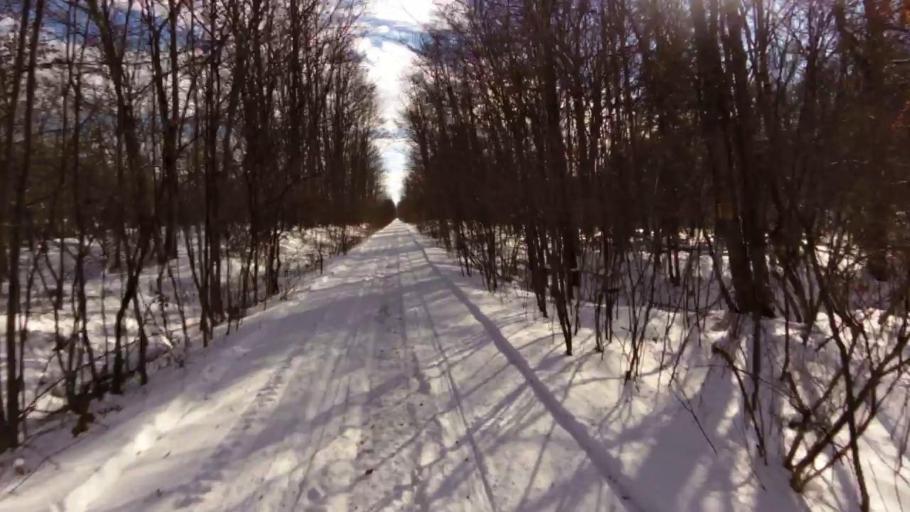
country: US
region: Pennsylvania
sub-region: McKean County
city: Foster Brook
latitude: 42.0557
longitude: -78.6371
